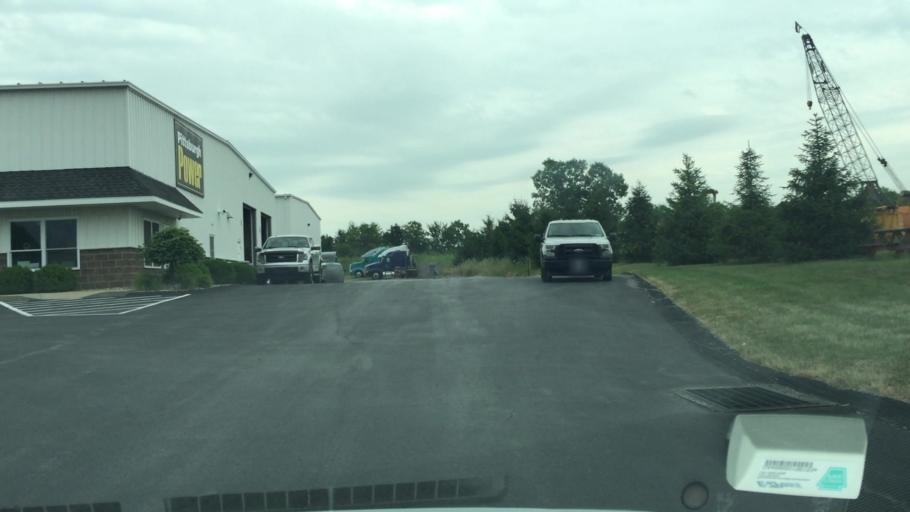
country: US
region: Pennsylvania
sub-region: Butler County
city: Saxonburg
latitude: 40.7330
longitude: -79.8456
